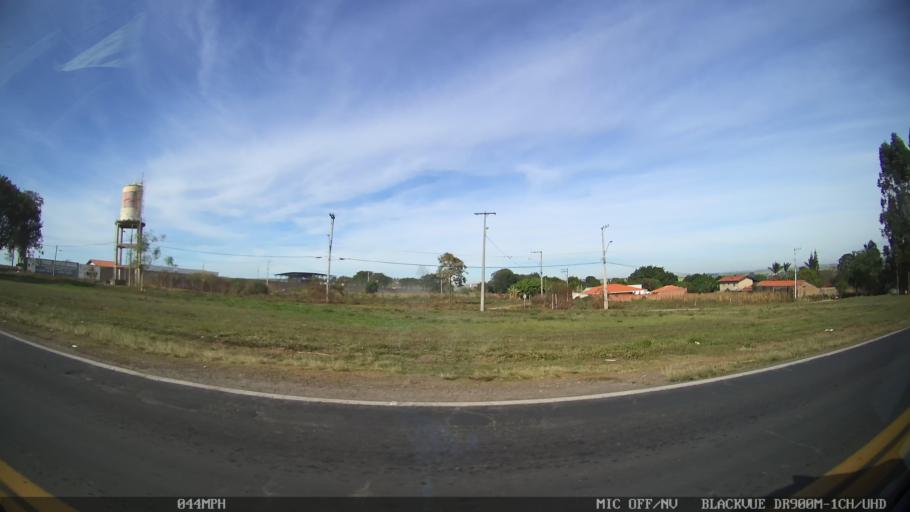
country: BR
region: Sao Paulo
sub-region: Rio Das Pedras
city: Rio das Pedras
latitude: -22.7970
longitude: -47.6036
